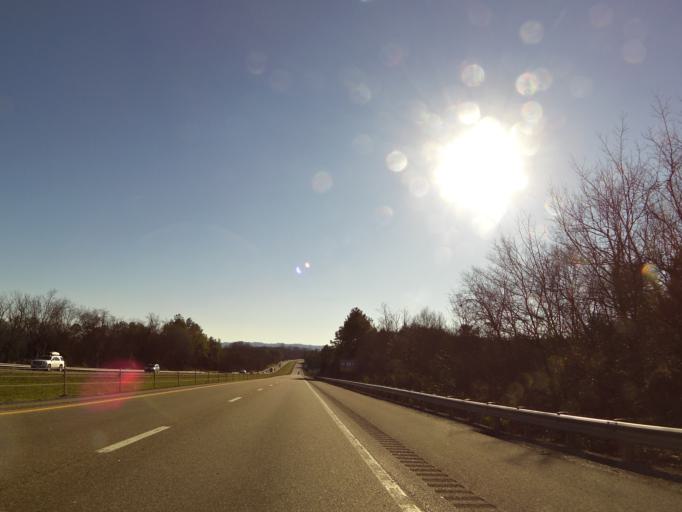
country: US
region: Tennessee
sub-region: Cocke County
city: Newport
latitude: 35.9650
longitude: -83.2202
